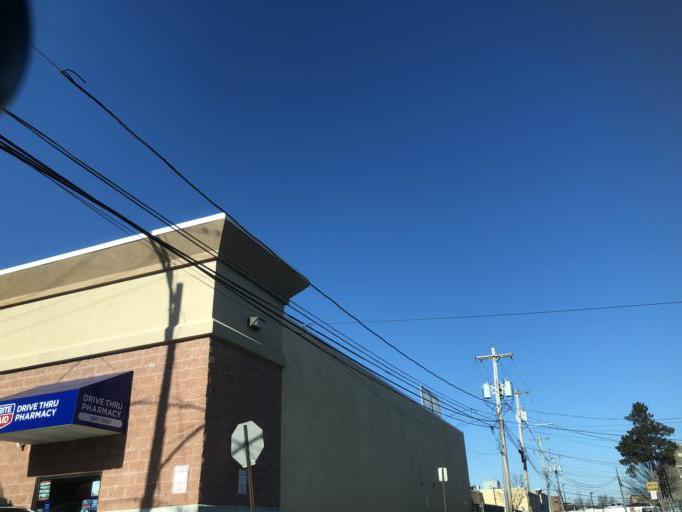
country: US
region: Pennsylvania
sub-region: Delaware County
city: Millbourne
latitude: 39.9578
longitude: -75.2571
